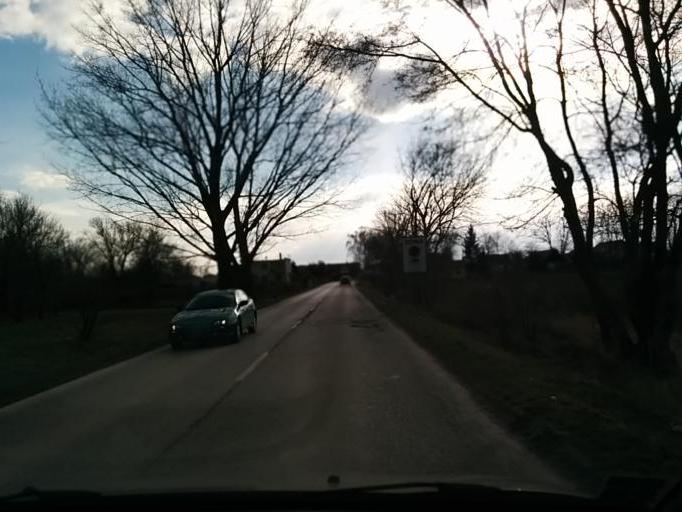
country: SK
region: Trnavsky
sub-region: Okres Trnava
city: Trnava
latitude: 48.3349
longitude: 17.5945
